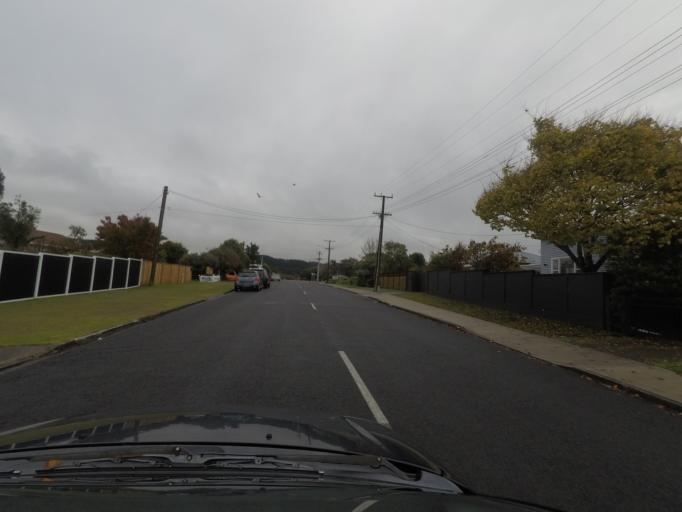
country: NZ
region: Auckland
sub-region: Auckland
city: Rosebank
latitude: -36.7598
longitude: 174.5925
